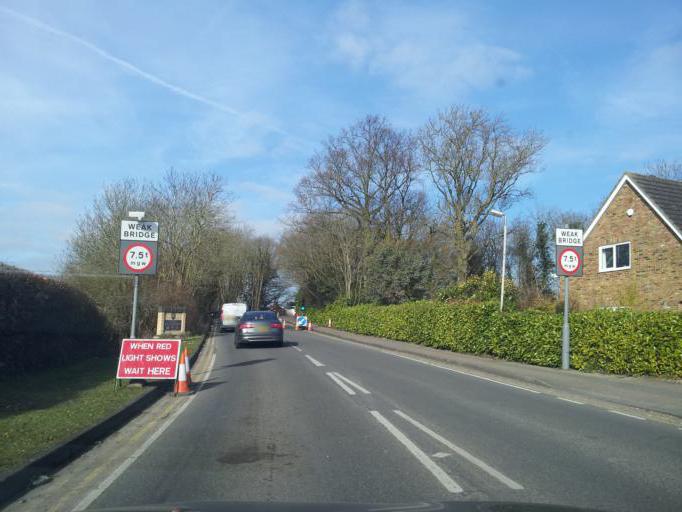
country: GB
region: England
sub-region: Hertfordshire
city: St Albans
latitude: 51.7489
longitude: -0.2896
